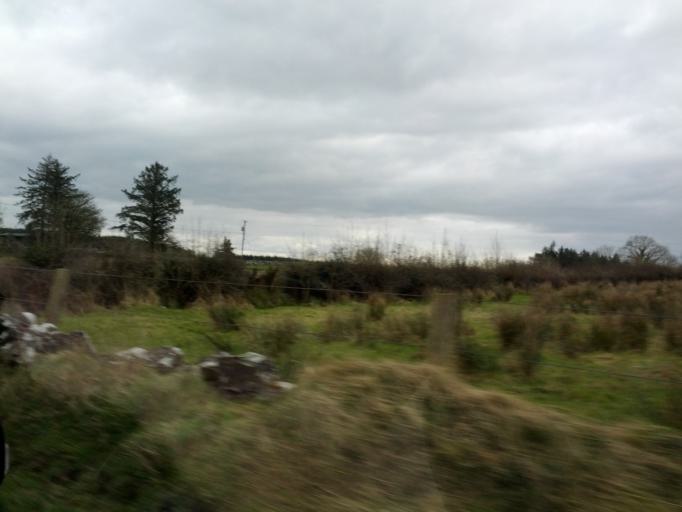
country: IE
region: Connaught
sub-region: County Galway
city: Athenry
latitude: 53.3734
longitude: -8.6376
